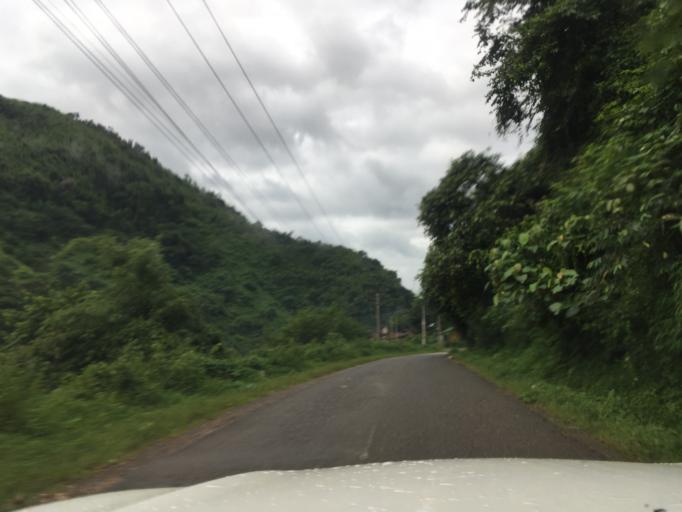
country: LA
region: Oudomxai
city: Muang La
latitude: 20.9892
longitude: 102.2276
